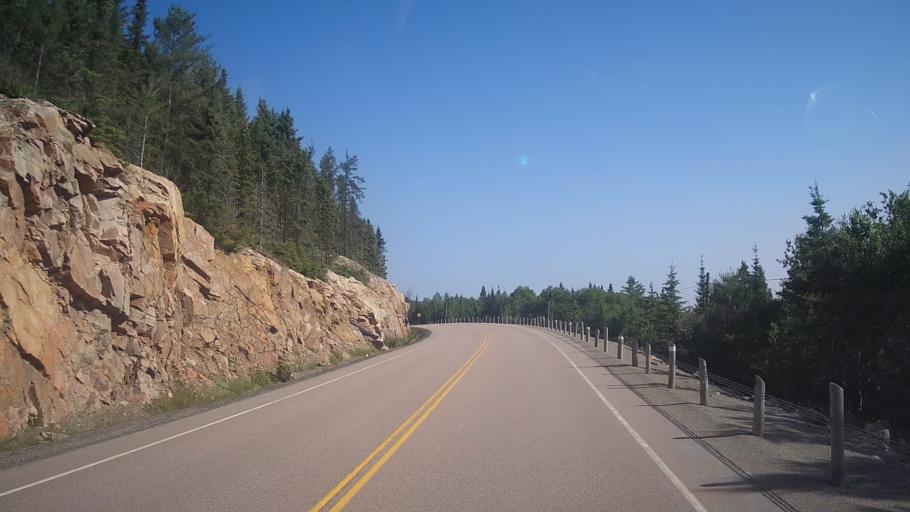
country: CA
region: Ontario
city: Rayside-Balfour
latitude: 47.0197
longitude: -81.6384
